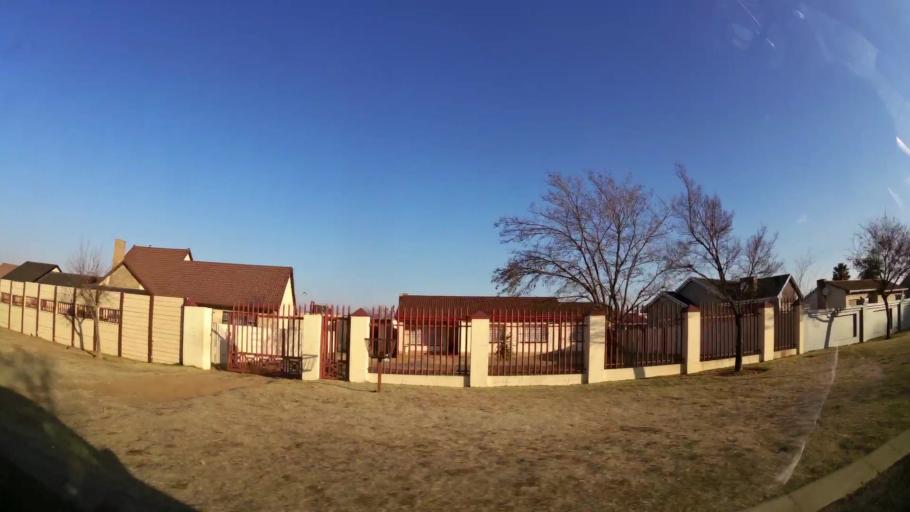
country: ZA
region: Gauteng
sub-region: West Rand District Municipality
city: Randfontein
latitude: -26.2058
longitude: 27.6499
